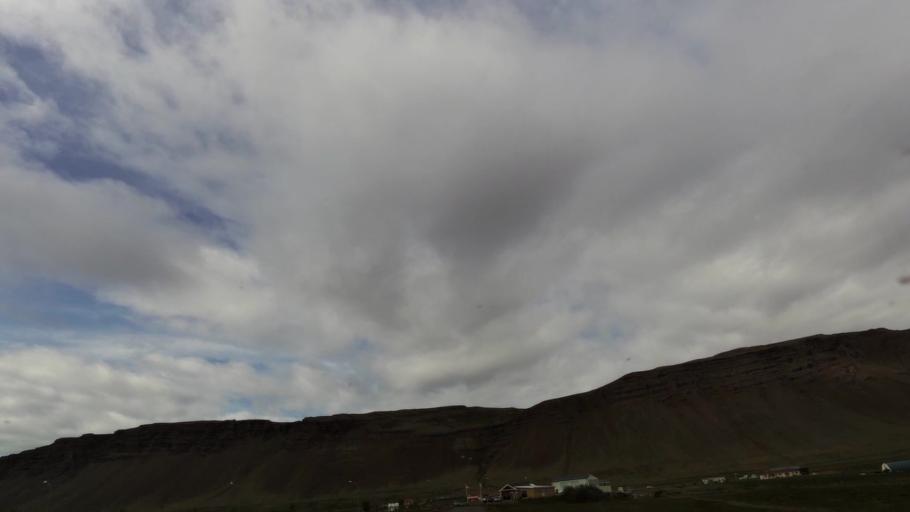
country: IS
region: West
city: Stykkisholmur
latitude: 65.4499
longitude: -22.2008
